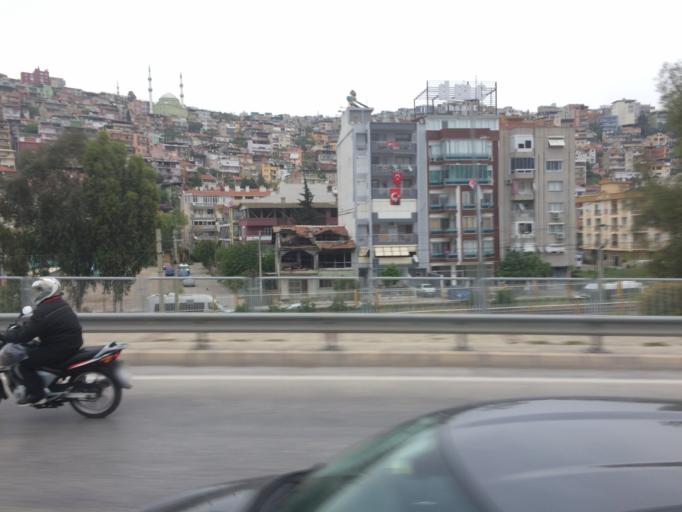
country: TR
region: Izmir
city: Karsiyaka
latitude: 38.4677
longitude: 27.1588
